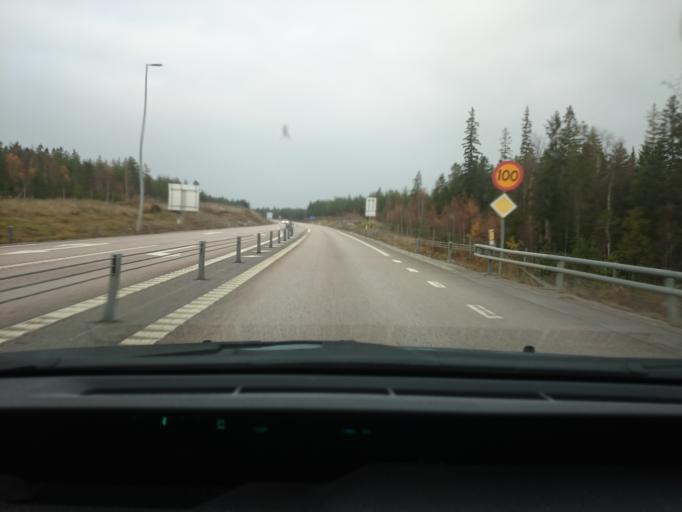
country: SE
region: Vaestmanland
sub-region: Sala Kommun
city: Sala
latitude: 59.9838
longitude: 16.4578
